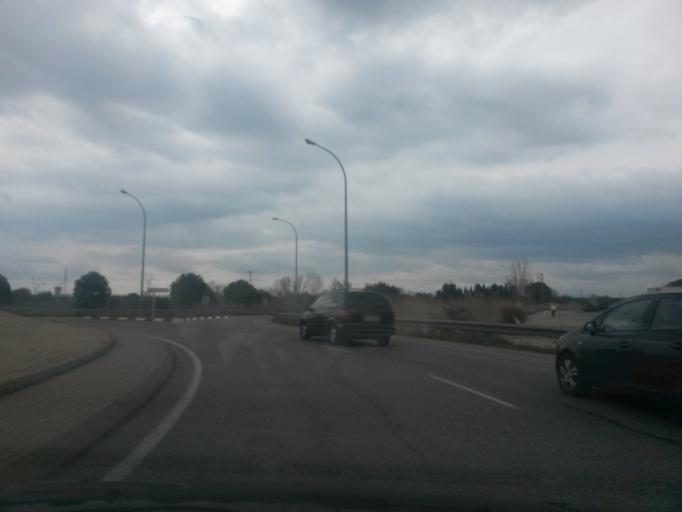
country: ES
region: Catalonia
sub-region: Provincia de Girona
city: Vila-sacra
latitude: 42.2621
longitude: 3.0361
